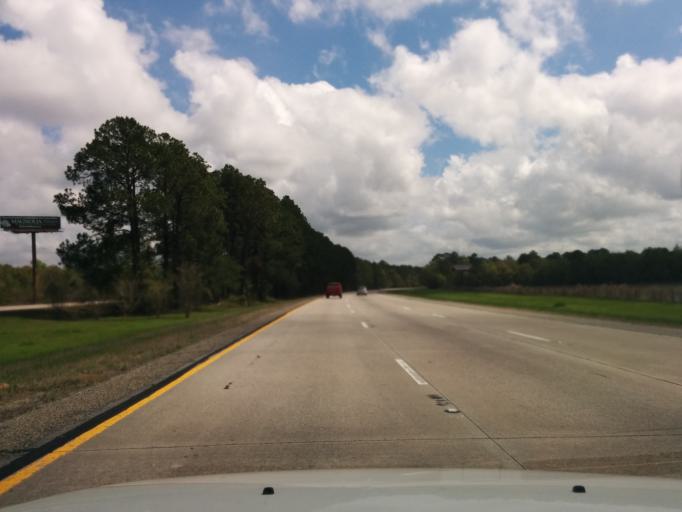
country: US
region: Georgia
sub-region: Bulloch County
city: Brooklet
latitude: 32.2549
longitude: -81.7055
